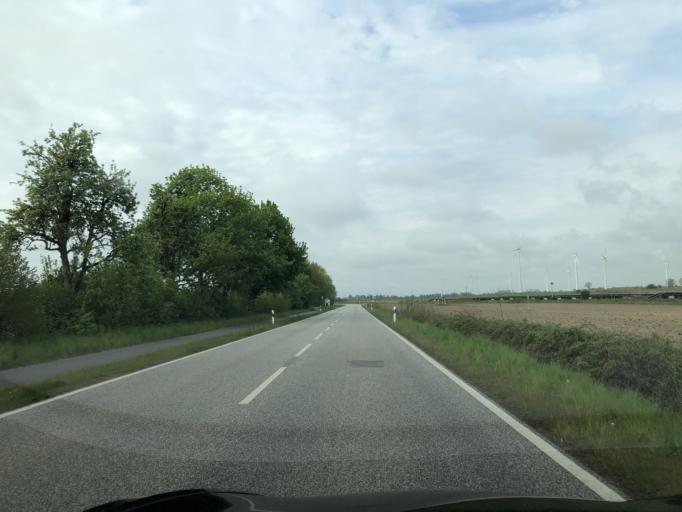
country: DE
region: Mecklenburg-Vorpommern
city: Lubz
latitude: 53.4950
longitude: 12.0386
